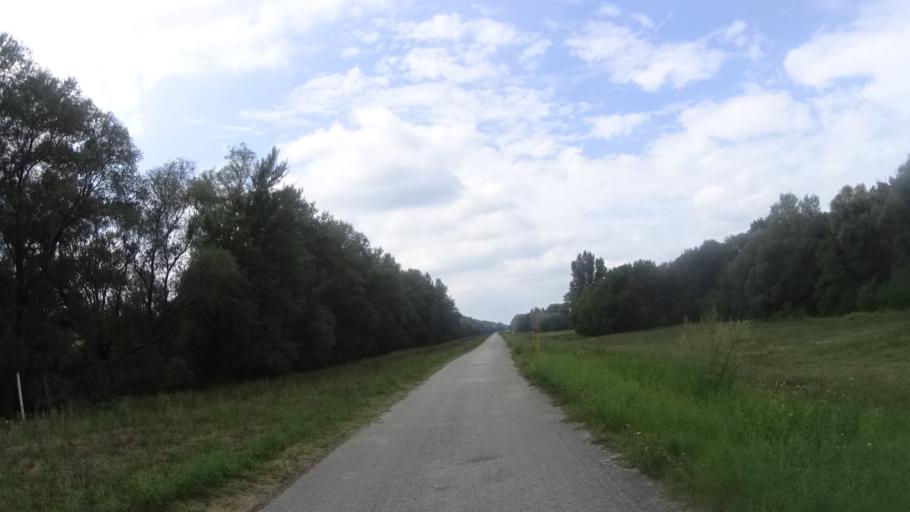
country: SK
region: Trnavsky
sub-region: Okres Dunajska Streda
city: Velky Meder
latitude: 47.7691
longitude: 17.7187
